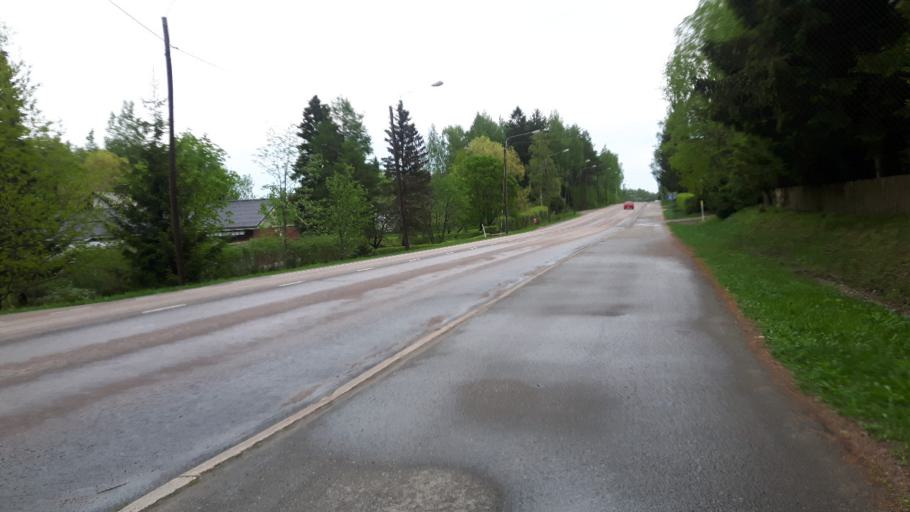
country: FI
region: Kymenlaakso
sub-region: Kotka-Hamina
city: Hamina
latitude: 60.5639
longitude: 27.1509
